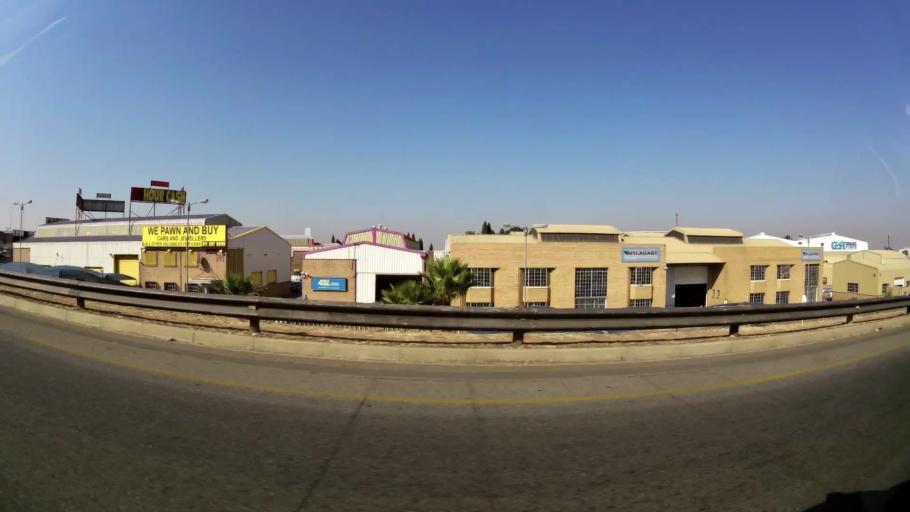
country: ZA
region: Gauteng
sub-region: Ekurhuleni Metropolitan Municipality
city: Boksburg
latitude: -26.1543
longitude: 28.2213
